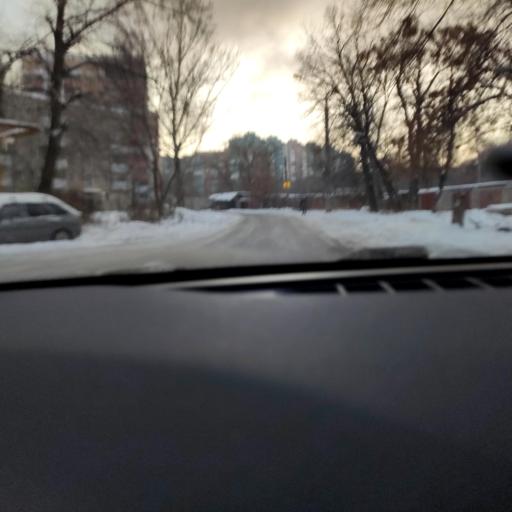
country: RU
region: Samara
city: Petra-Dubrava
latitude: 53.2789
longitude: 50.2697
